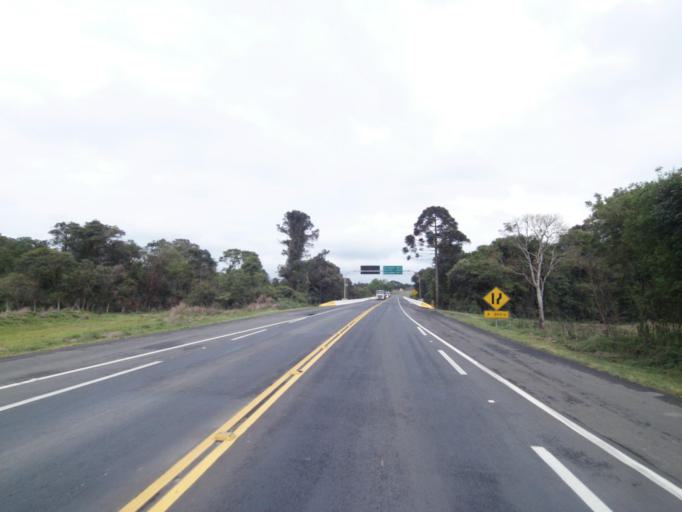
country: BR
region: Parana
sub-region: Irati
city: Irati
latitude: -25.4551
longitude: -50.6233
